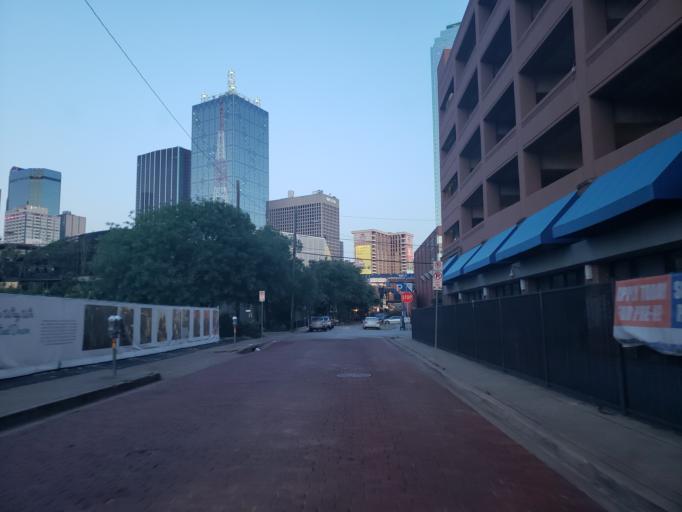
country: US
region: Texas
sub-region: Dallas County
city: Dallas
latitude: 32.7841
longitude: -96.8066
